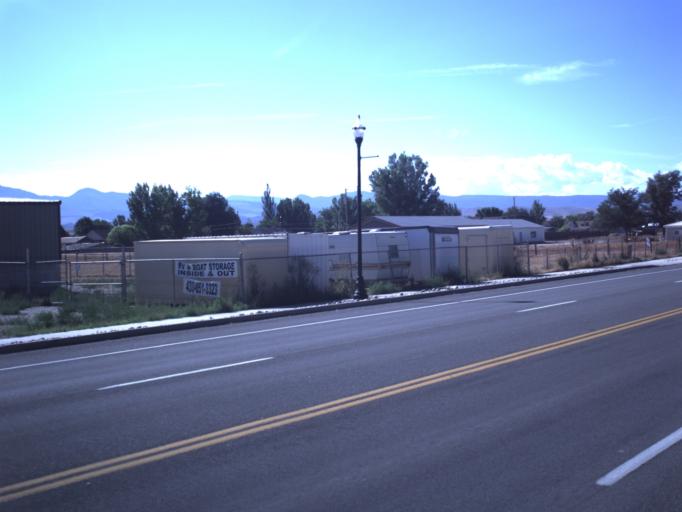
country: US
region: Utah
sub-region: Sanpete County
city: Centerfield
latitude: 39.1302
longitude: -111.8192
